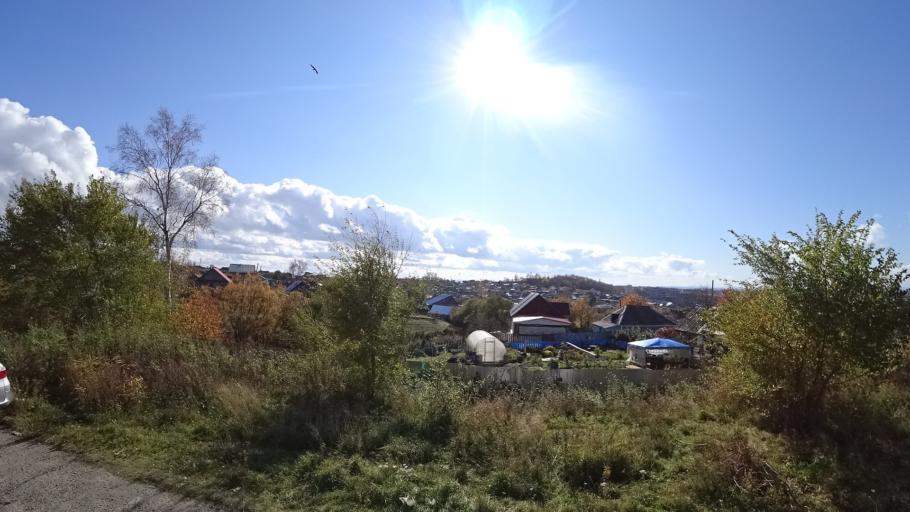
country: RU
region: Khabarovsk Krai
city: Amursk
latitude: 50.2379
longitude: 136.9166
